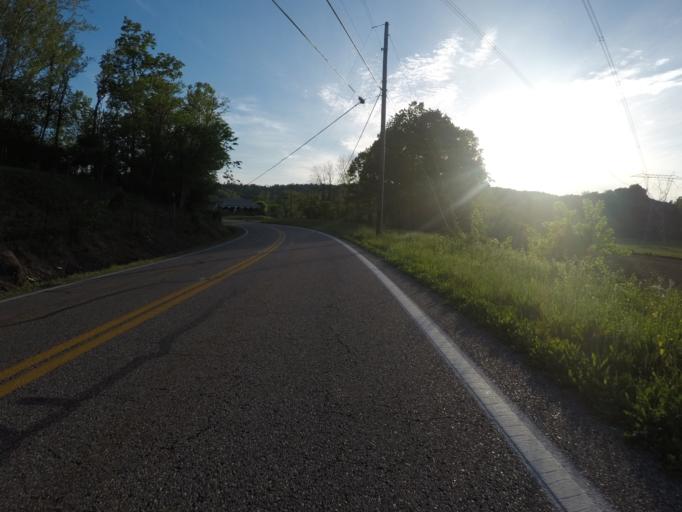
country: US
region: West Virginia
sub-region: Cabell County
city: Huntington
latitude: 38.5212
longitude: -82.4714
